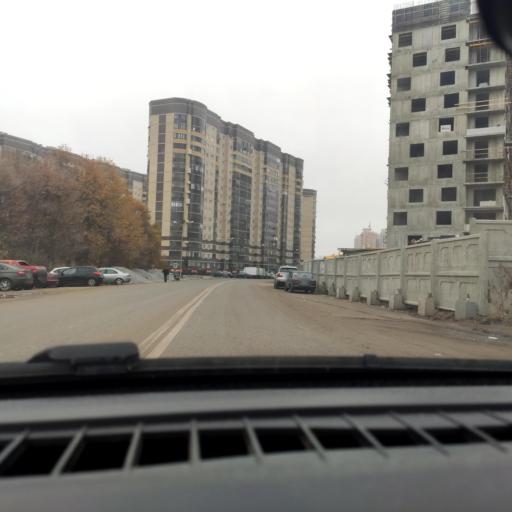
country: RU
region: Voronezj
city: Podgornoye
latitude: 51.7171
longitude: 39.1913
